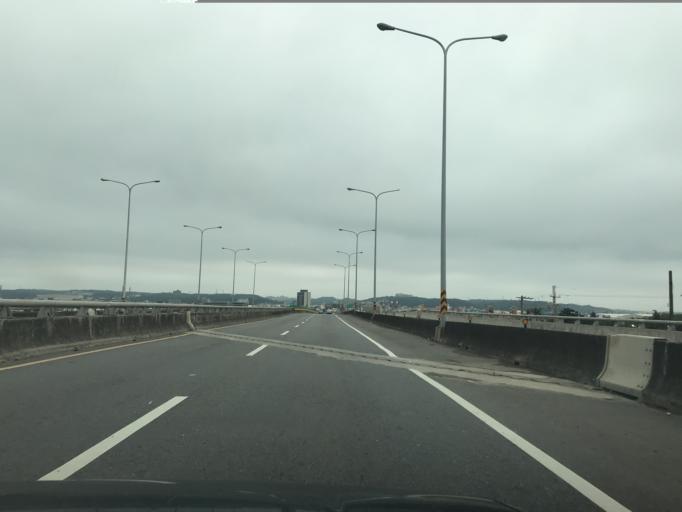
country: TW
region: Taiwan
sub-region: Hsinchu
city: Hsinchu
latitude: 24.8058
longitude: 120.9187
